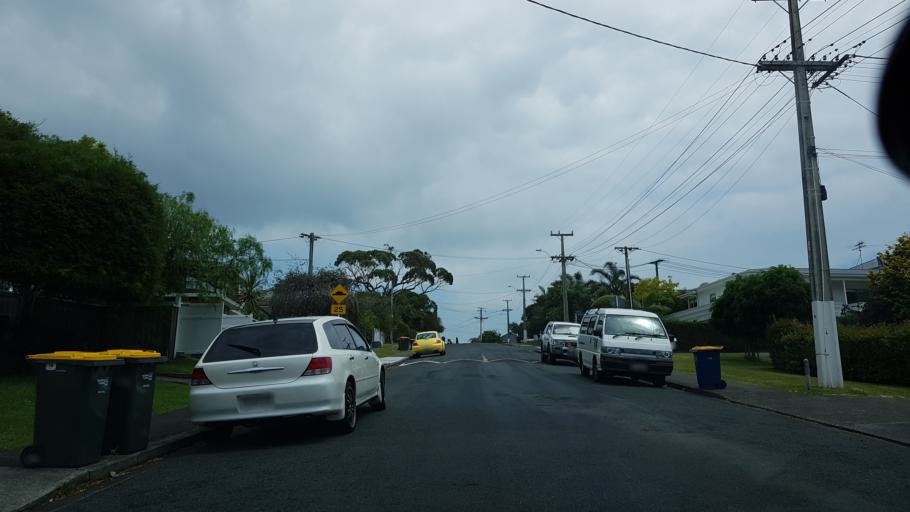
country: NZ
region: Auckland
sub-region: Auckland
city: North Shore
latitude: -36.7983
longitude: 174.7736
